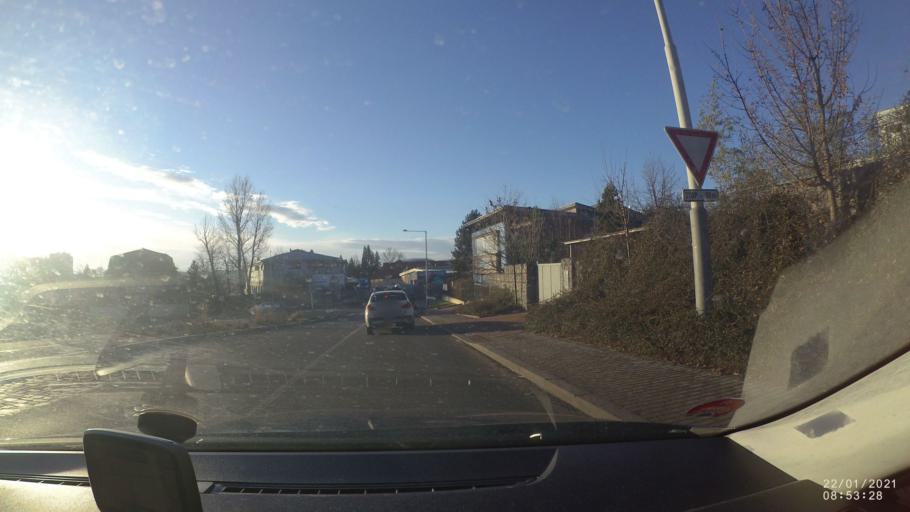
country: CZ
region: Praha
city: Prague
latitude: 50.1199
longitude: 14.4124
